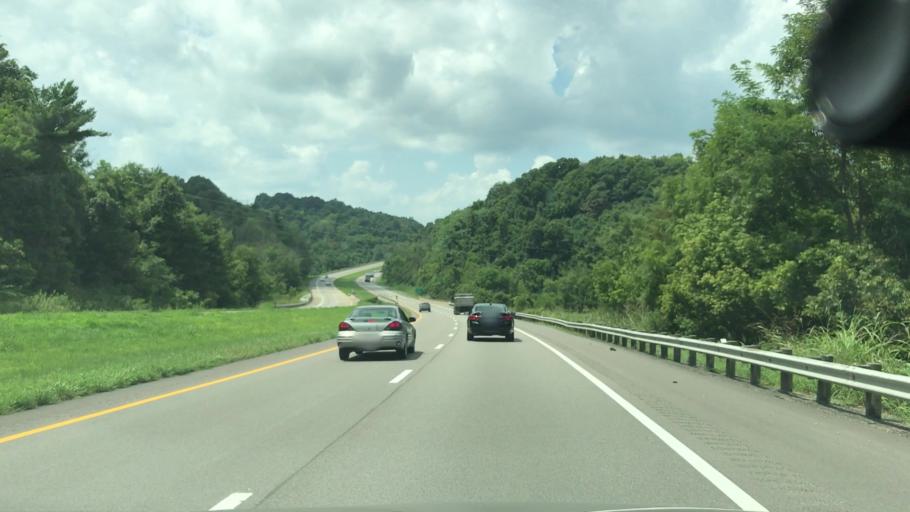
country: US
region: Ohio
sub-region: Gallia County
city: Gallipolis
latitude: 38.8396
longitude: -82.1789
